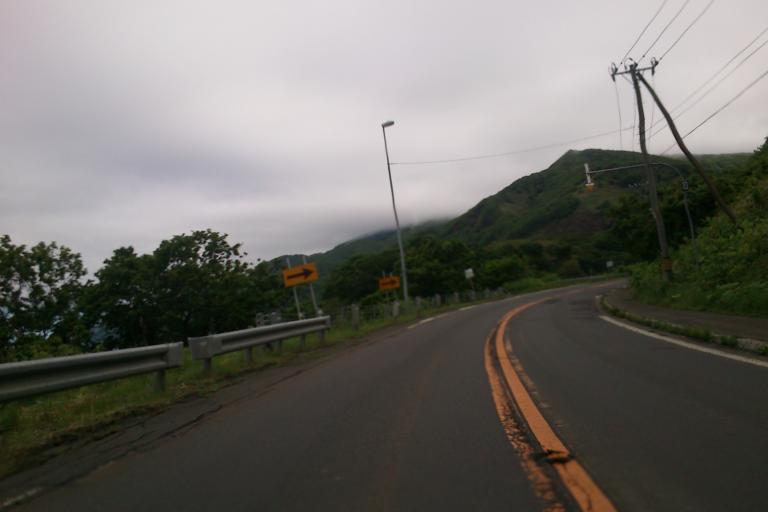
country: JP
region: Hokkaido
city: Ishikari
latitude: 43.4104
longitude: 141.4302
